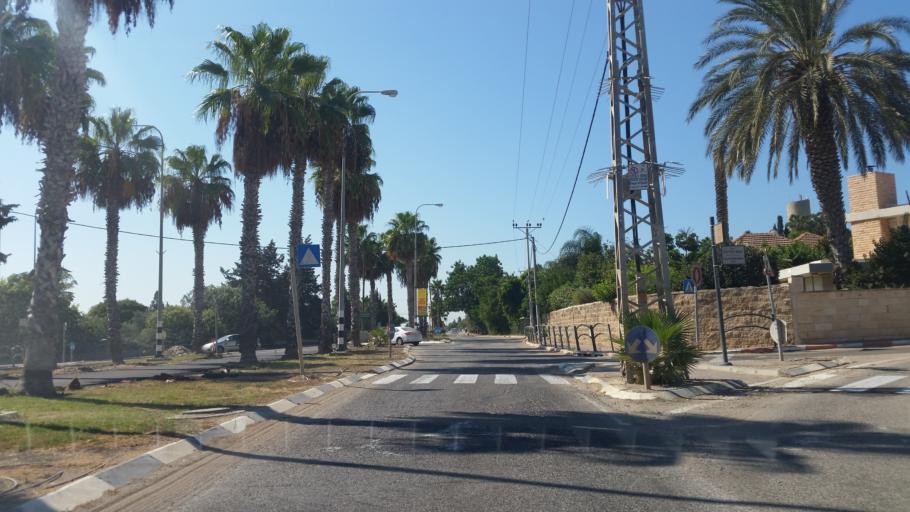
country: IL
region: Haifa
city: `Atlit
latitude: 32.6917
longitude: 34.9452
